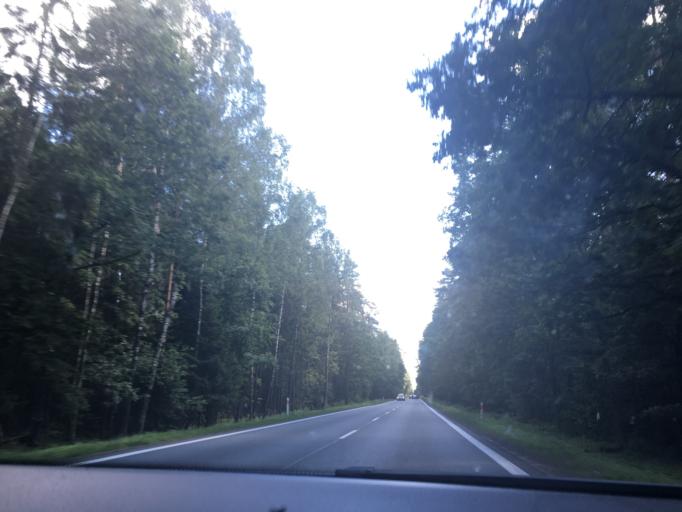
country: PL
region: Podlasie
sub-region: Powiat bialostocki
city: Wasilkow
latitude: 53.2980
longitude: 23.1243
